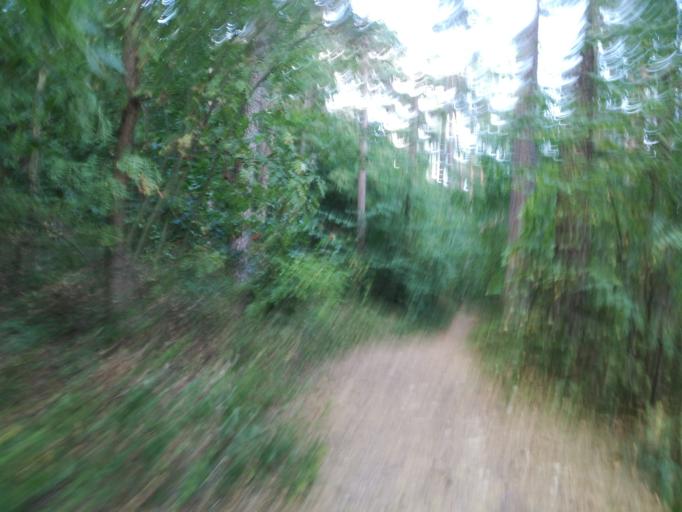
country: DE
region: Bavaria
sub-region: Regierungsbezirk Mittelfranken
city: Seukendorf
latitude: 49.4730
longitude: 10.9149
